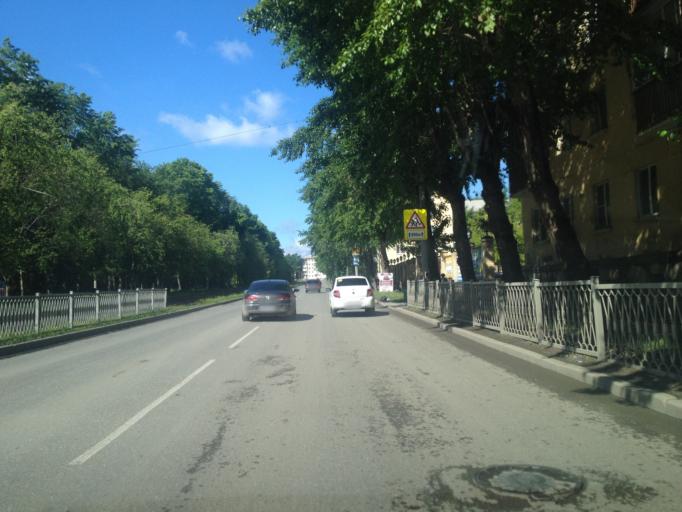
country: RU
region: Sverdlovsk
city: Sovkhoznyy
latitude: 56.7723
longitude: 60.6084
